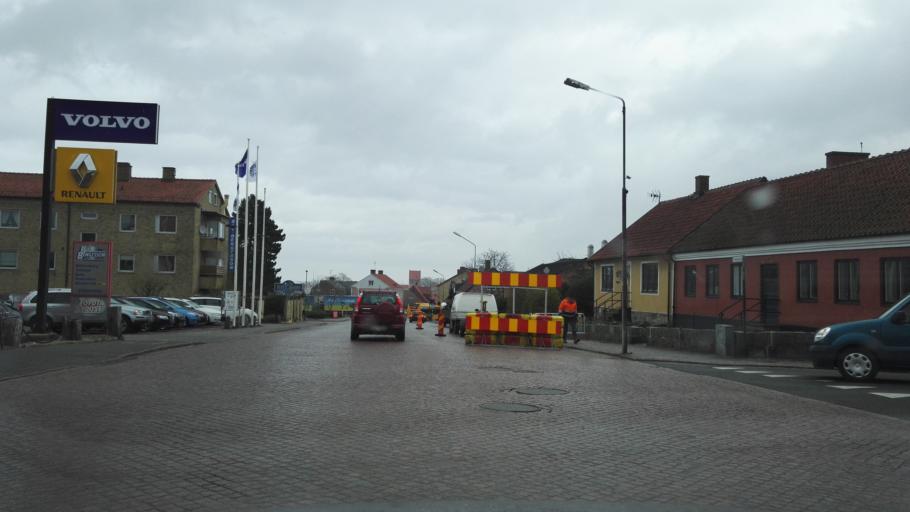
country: SE
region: Skane
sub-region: Simrishamns Kommun
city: Simrishamn
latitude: 55.5552
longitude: 14.3392
